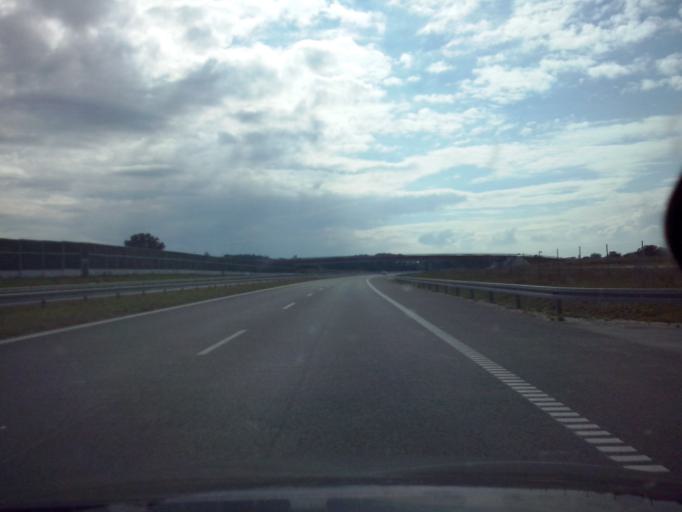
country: PL
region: Lesser Poland Voivodeship
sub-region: Powiat tarnowski
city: Lisia Gora
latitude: 50.0571
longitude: 21.0337
